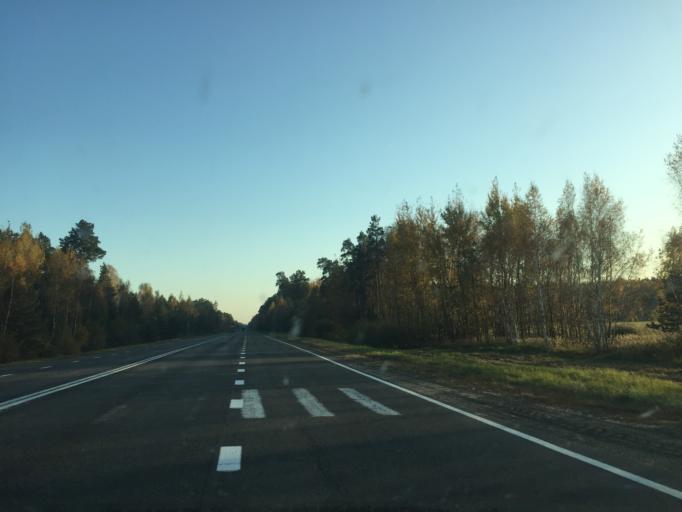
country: BY
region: Mogilev
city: Poselok Voskhod
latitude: 53.7138
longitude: 30.3678
